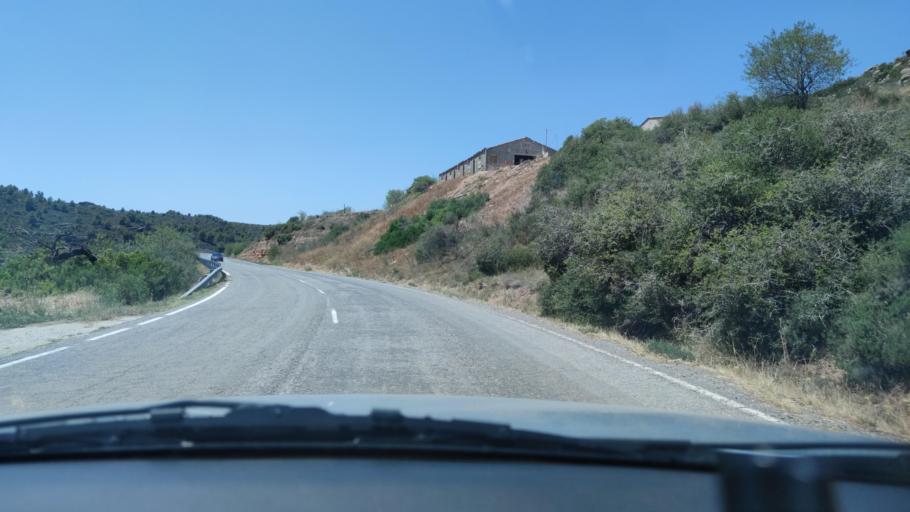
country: ES
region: Catalonia
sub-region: Provincia de Lleida
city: el Cogul
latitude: 41.4175
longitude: 0.6783
